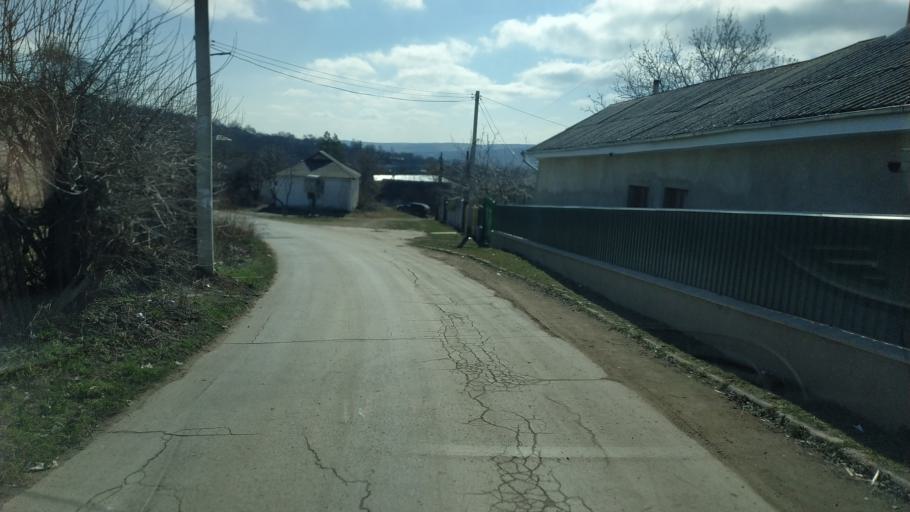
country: MD
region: Straseni
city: Straseni
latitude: 47.0196
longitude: 28.5435
